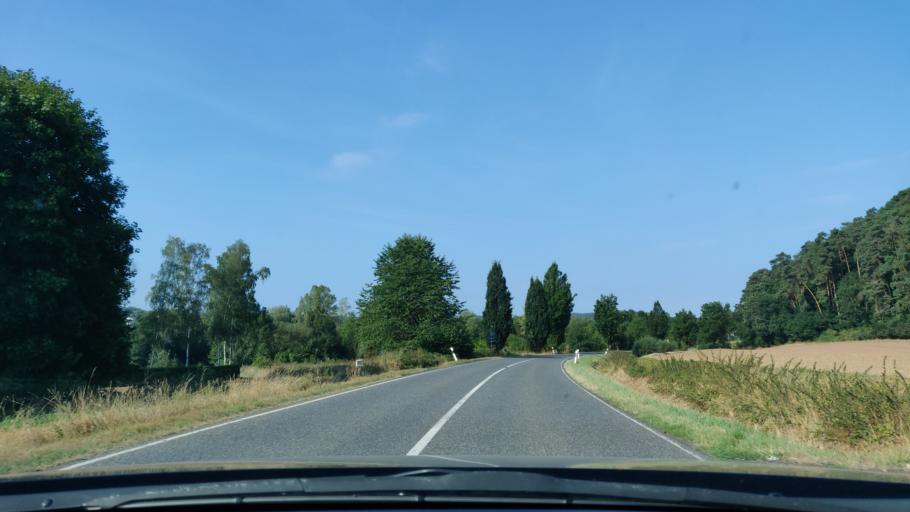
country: DE
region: Hesse
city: Fritzlar
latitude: 51.1294
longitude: 9.2317
